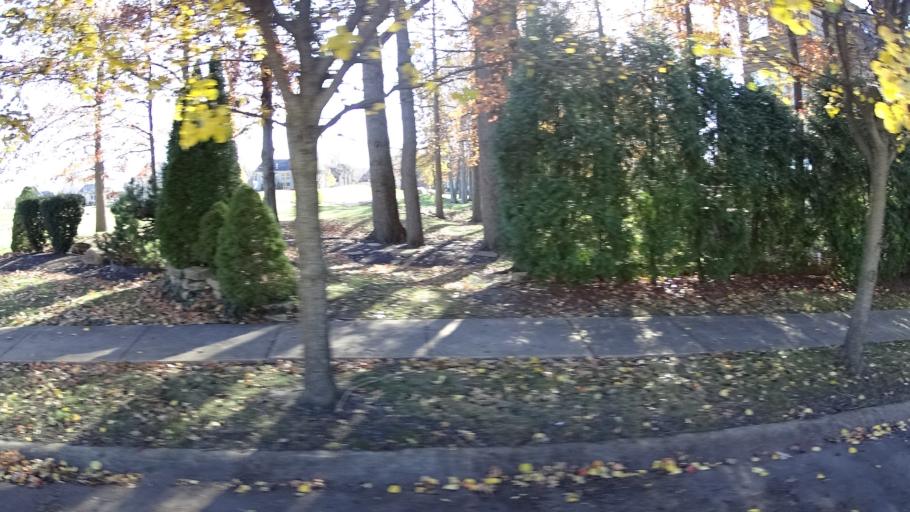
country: US
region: Ohio
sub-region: Lorain County
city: North Ridgeville
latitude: 41.4222
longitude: -81.9935
